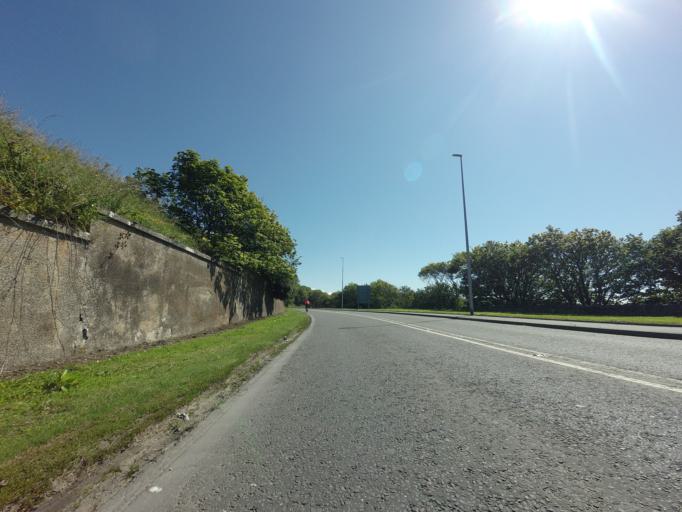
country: GB
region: Scotland
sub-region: Aberdeenshire
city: Macduff
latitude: 57.6622
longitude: -2.5119
